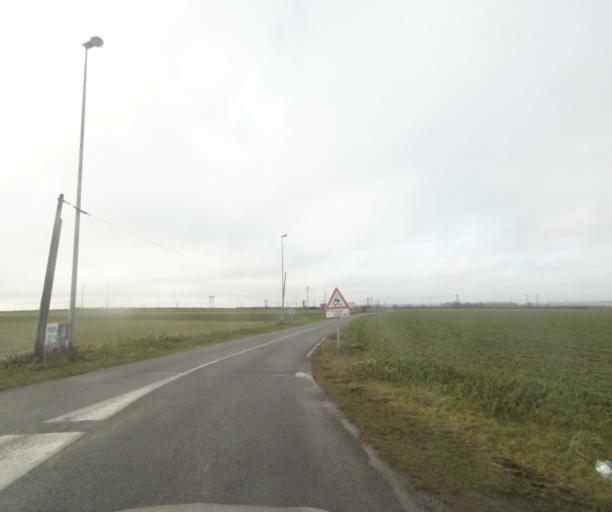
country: FR
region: Nord-Pas-de-Calais
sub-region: Departement du Nord
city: Famars
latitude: 50.3137
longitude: 3.5130
